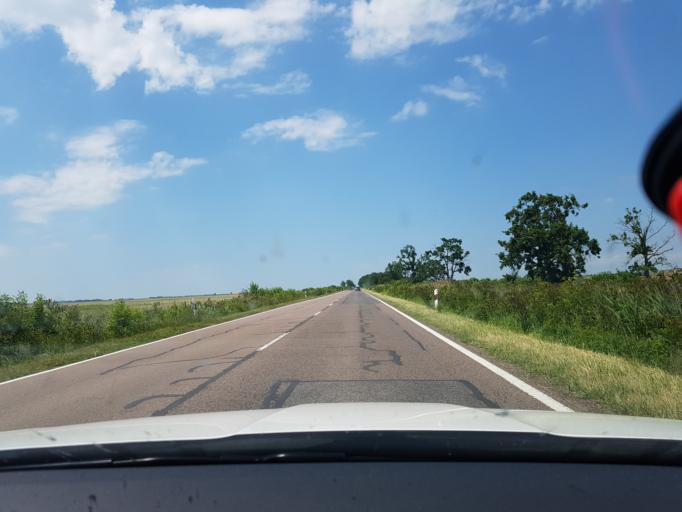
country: HU
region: Hajdu-Bihar
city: Hortobagy
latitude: 47.5842
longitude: 21.1238
